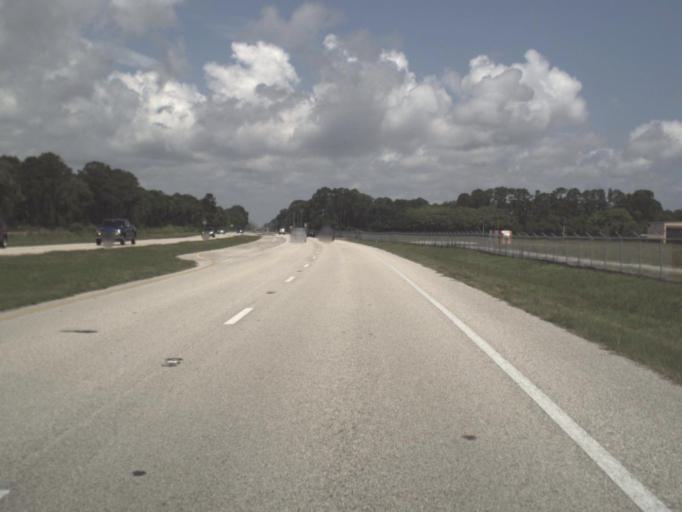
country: US
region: Florida
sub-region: Saint Johns County
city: Villano Beach
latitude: 29.9674
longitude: -81.3515
